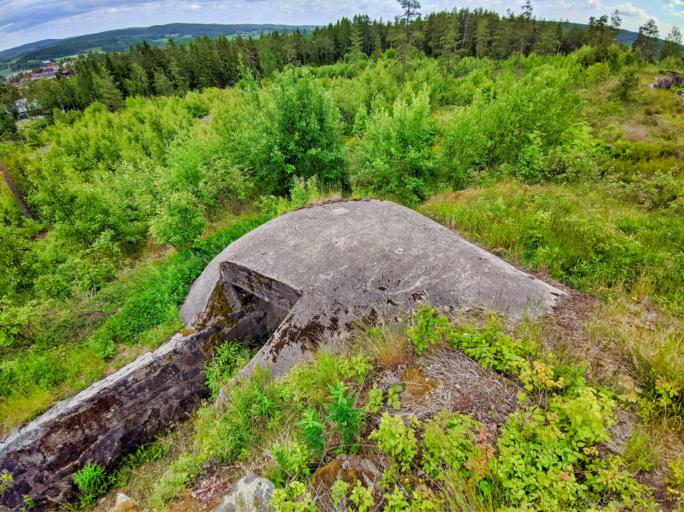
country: NO
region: Ostfold
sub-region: Eidsberg
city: Mysen
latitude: 59.5600
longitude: 11.3422
